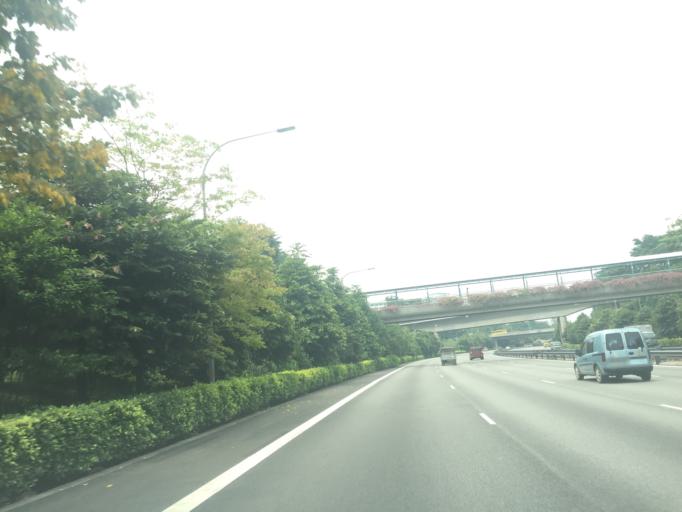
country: MY
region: Johor
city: Johor Bahru
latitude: 1.3876
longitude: 103.7426
